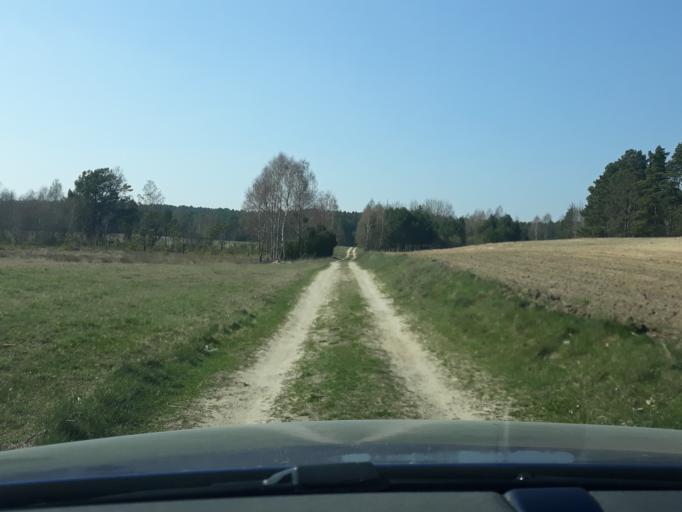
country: PL
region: Pomeranian Voivodeship
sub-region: Powiat bytowski
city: Lipnica
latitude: 53.8601
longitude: 17.4374
